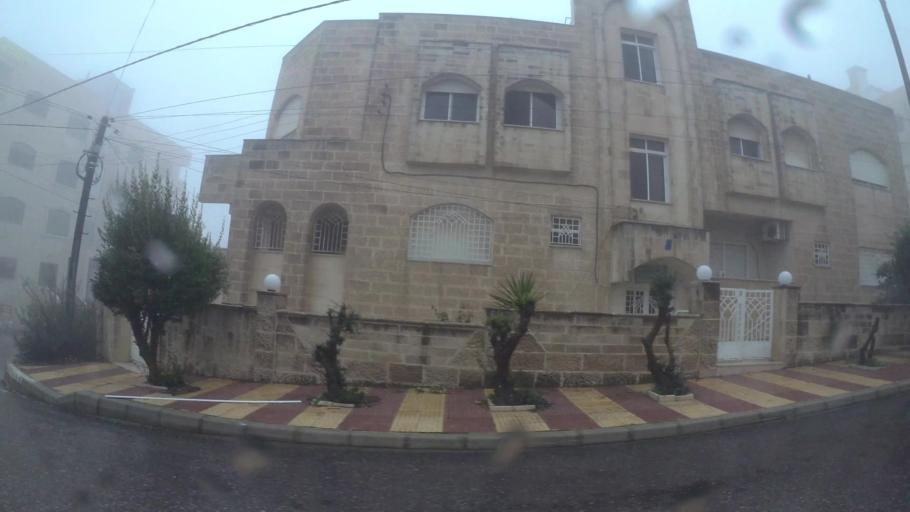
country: JO
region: Amman
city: Al Jubayhah
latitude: 32.0058
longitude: 35.8911
